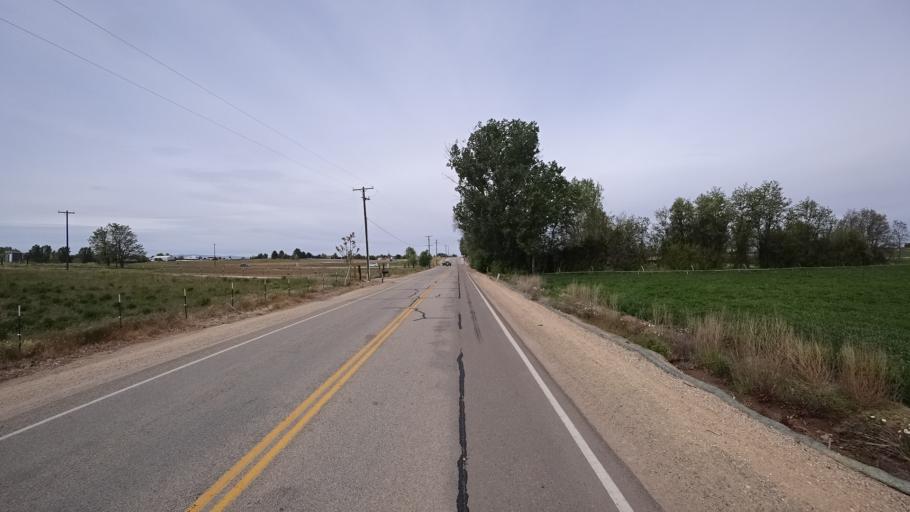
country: US
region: Idaho
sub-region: Ada County
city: Meridian
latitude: 43.5611
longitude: -116.4119
